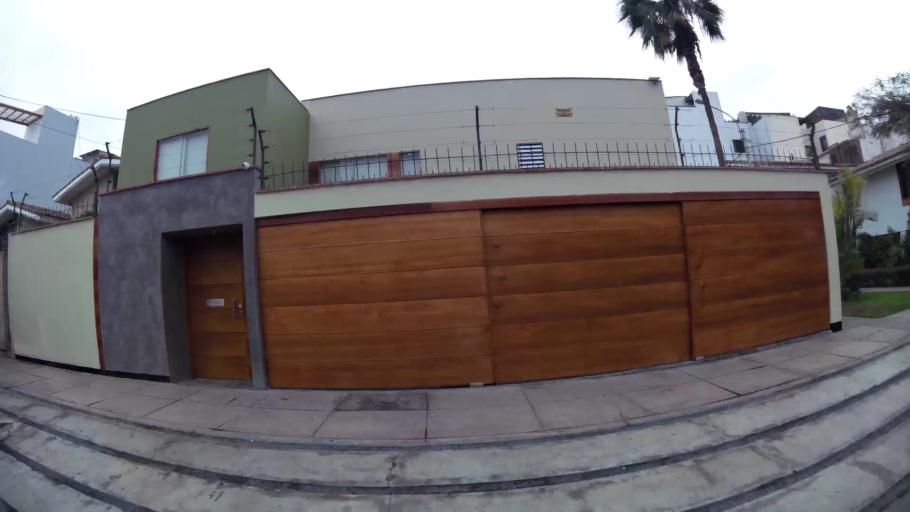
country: PE
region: Lima
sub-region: Lima
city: Surco
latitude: -12.1322
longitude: -77.0117
